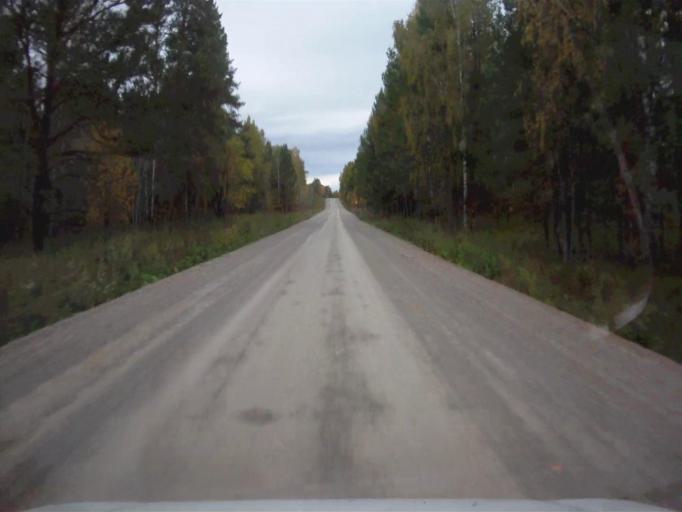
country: RU
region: Chelyabinsk
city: Nyazepetrovsk
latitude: 56.0762
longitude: 59.4262
